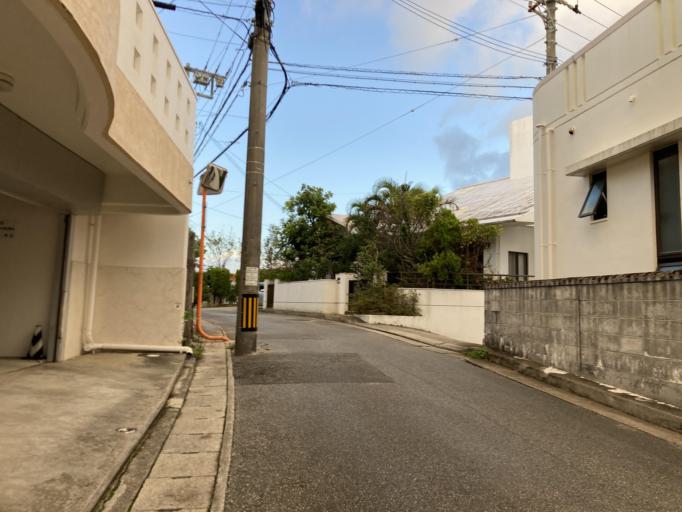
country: JP
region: Okinawa
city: Naha-shi
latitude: 26.2236
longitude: 127.7234
